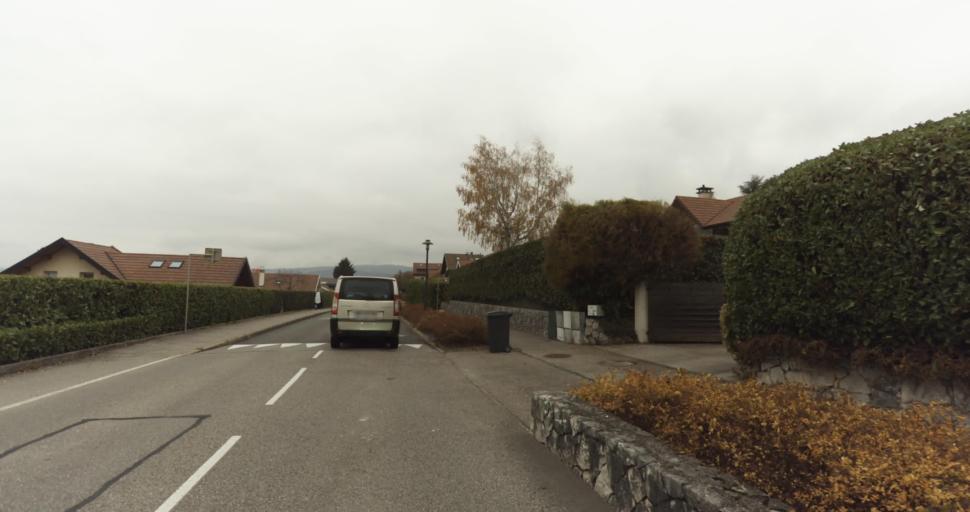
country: FR
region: Rhone-Alpes
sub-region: Departement de la Haute-Savoie
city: Annecy-le-Vieux
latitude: 45.9209
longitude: 6.1391
